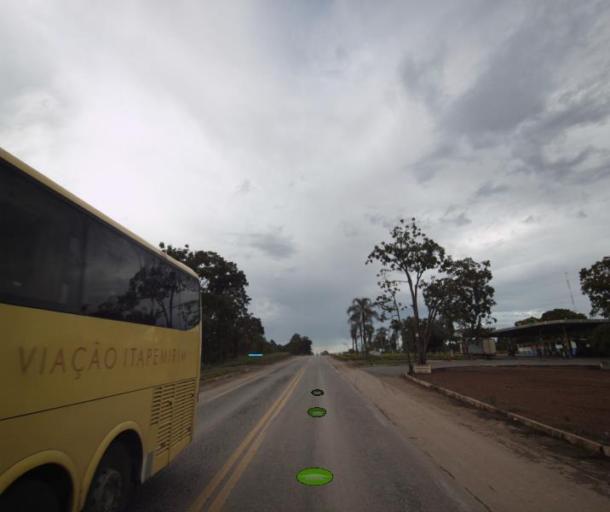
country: BR
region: Goias
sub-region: Porangatu
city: Porangatu
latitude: -13.5965
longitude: -49.0418
